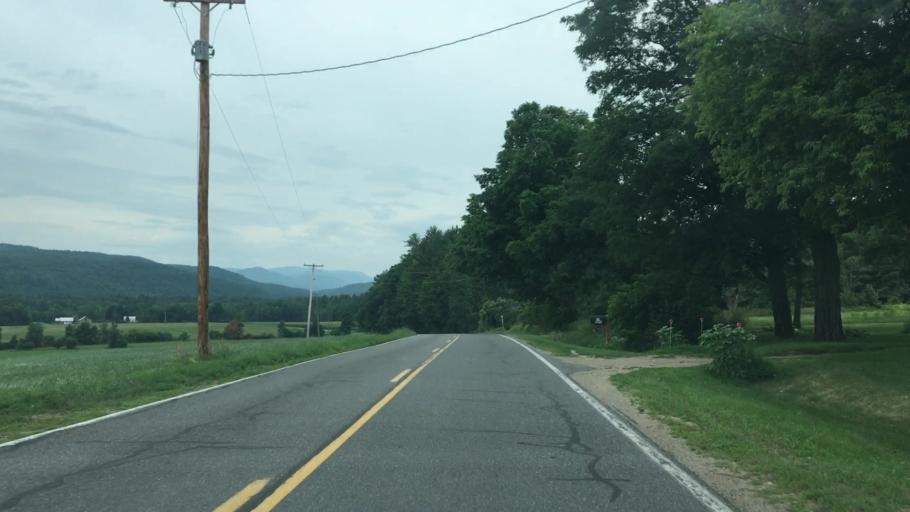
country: US
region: New York
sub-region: Clinton County
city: Peru
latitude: 44.5375
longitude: -73.5720
